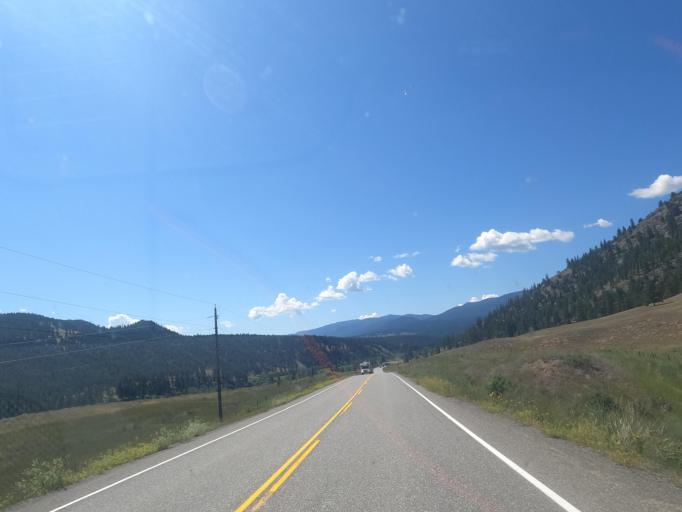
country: CA
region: British Columbia
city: Cache Creek
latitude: 50.8176
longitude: -121.5806
